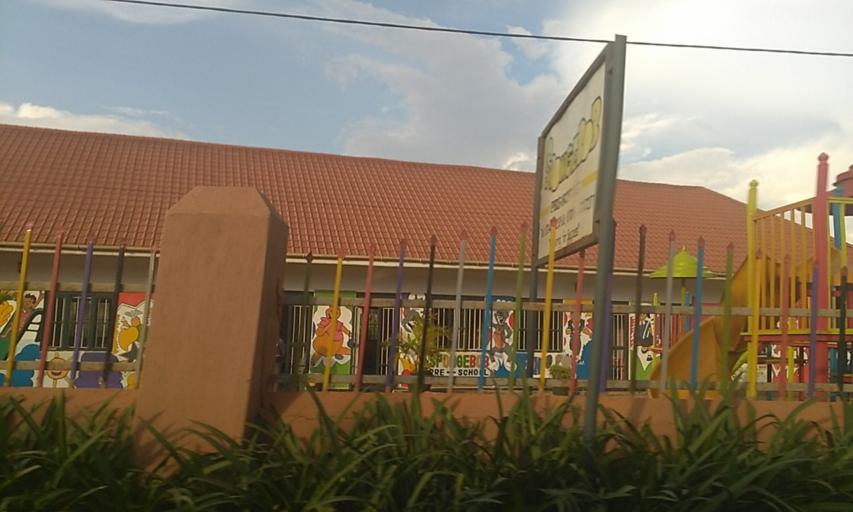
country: UG
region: Central Region
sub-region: Wakiso District
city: Kajansi
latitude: 0.2688
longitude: 32.5262
